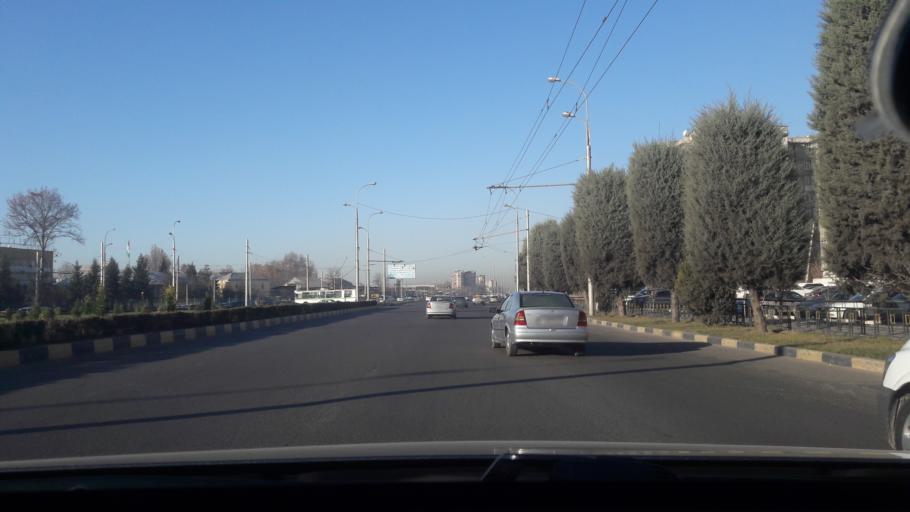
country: TJ
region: Dushanbe
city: Dushanbe
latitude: 38.5587
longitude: 68.7625
